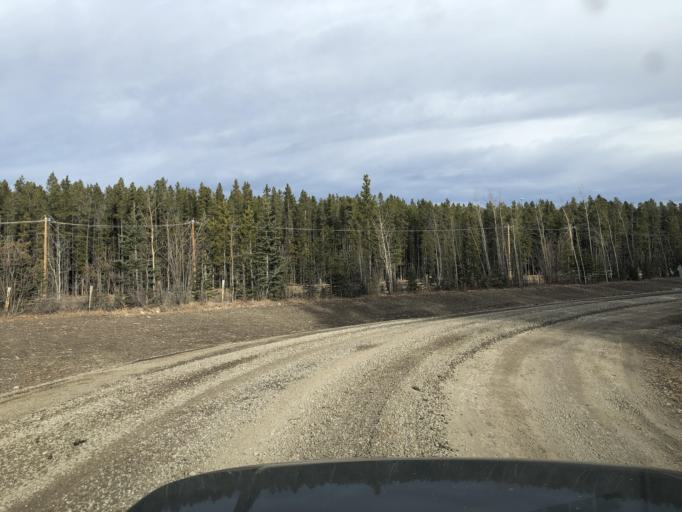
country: CA
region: Alberta
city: Cochrane
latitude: 50.9208
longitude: -114.6018
